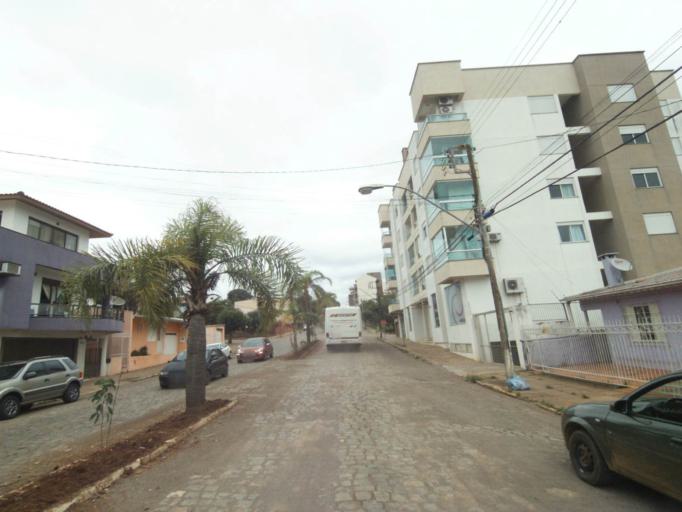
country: BR
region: Rio Grande do Sul
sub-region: Lagoa Vermelha
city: Lagoa Vermelha
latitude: -28.2082
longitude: -51.5222
